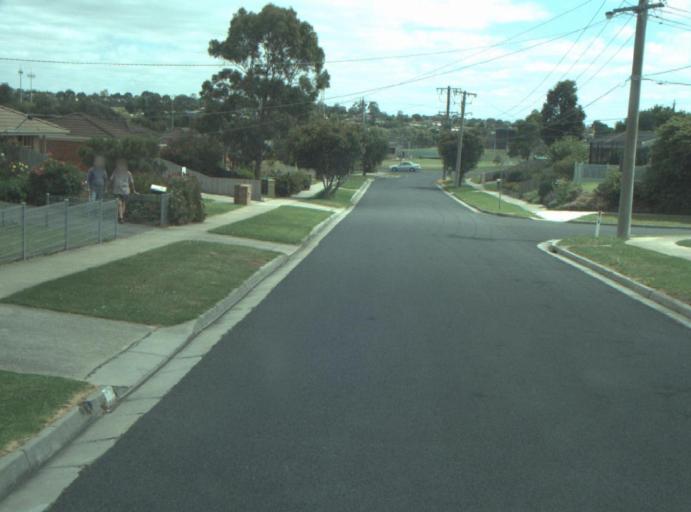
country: AU
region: Victoria
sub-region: Greater Geelong
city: Wandana Heights
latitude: -38.2022
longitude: 144.3245
